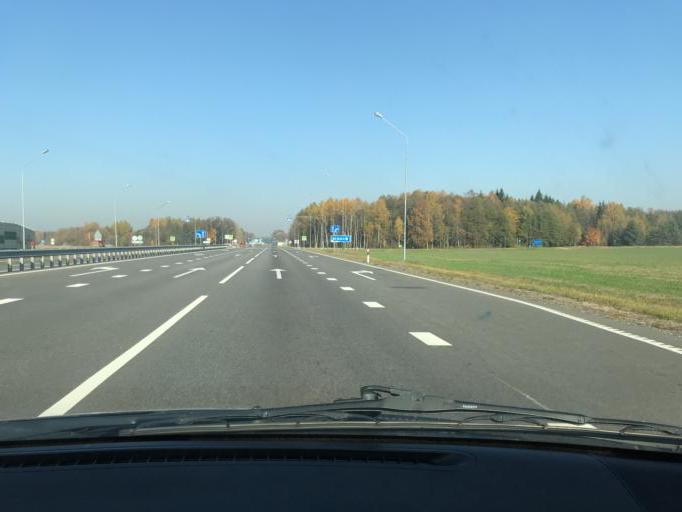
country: BY
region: Minsk
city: Slutsk
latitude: 53.2705
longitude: 27.5502
